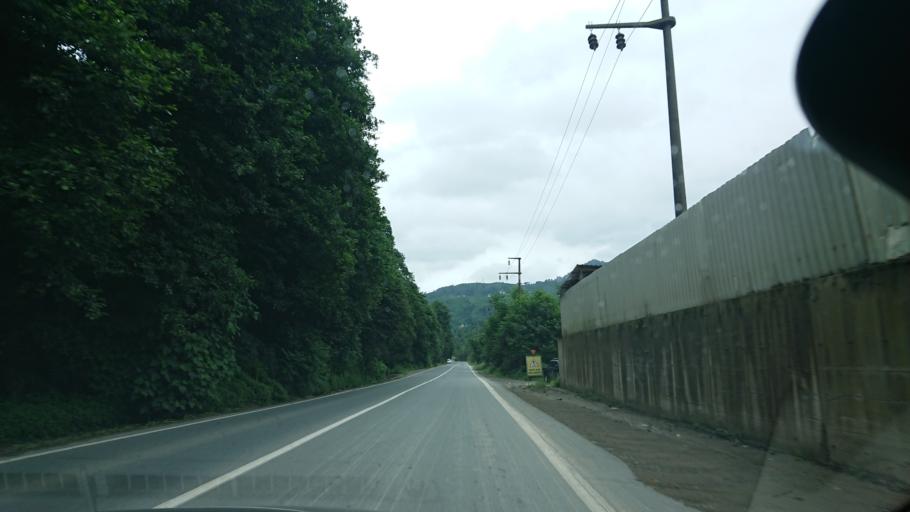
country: TR
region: Rize
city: Gundogdu
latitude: 41.0170
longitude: 40.5696
